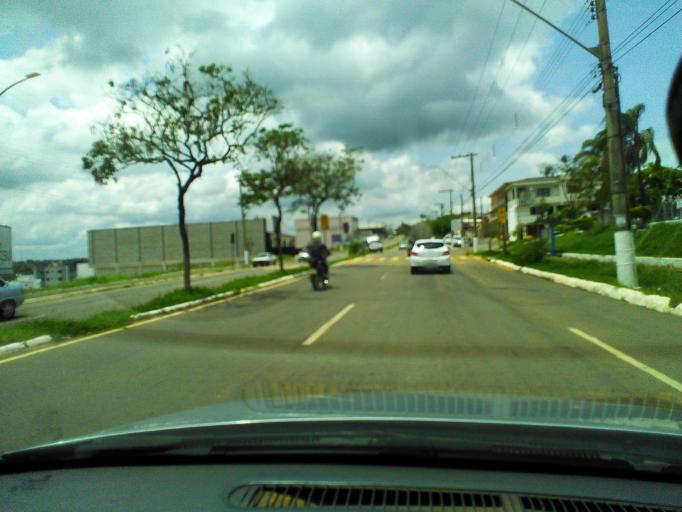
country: BR
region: Minas Gerais
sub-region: Tres Coracoes
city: Tres Coracoes
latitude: -21.6809
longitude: -45.2665
